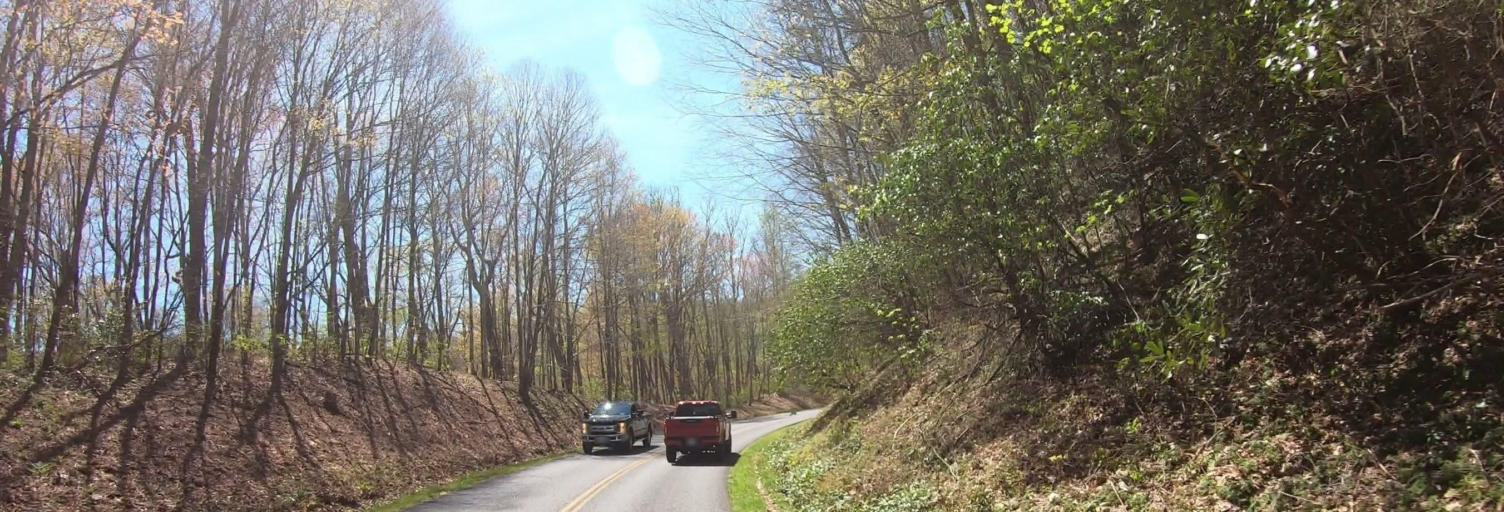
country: US
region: North Carolina
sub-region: Swain County
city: Cherokee
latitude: 35.5197
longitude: -83.2610
